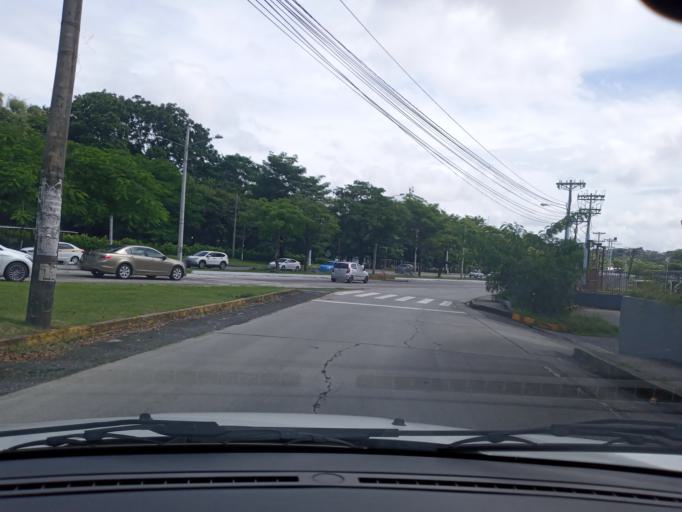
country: PA
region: Panama
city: Panama
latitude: 9.0283
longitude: -79.5193
